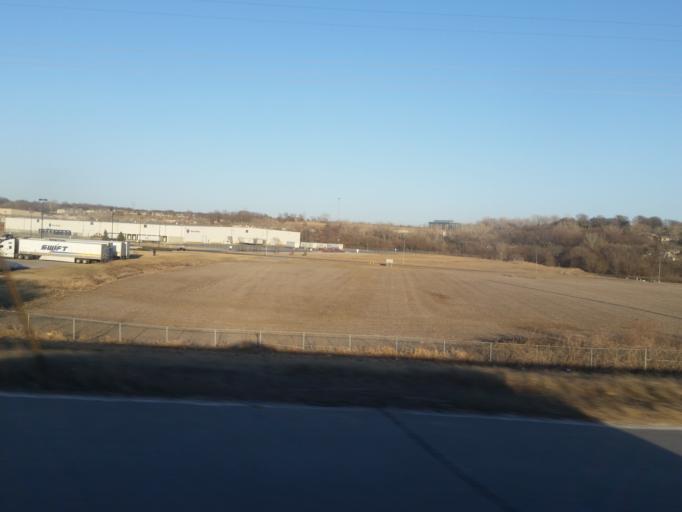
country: US
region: Nebraska
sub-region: Sarpy County
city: Offutt Air Force Base
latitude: 41.1537
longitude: -95.9387
